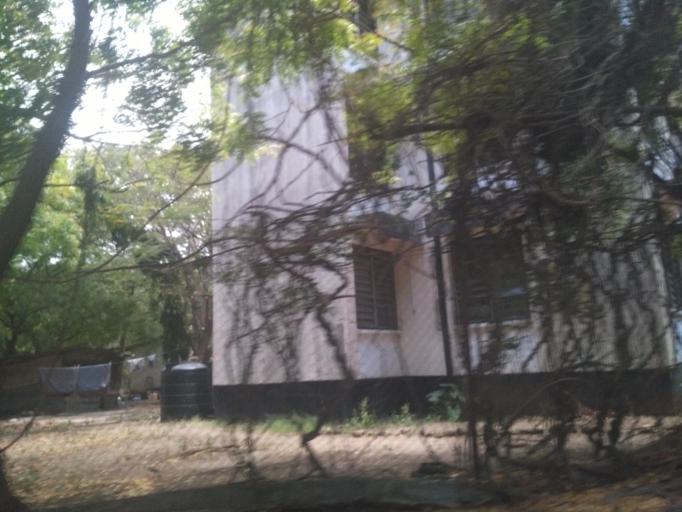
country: TZ
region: Dar es Salaam
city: Magomeni
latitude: -6.7519
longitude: 39.2741
